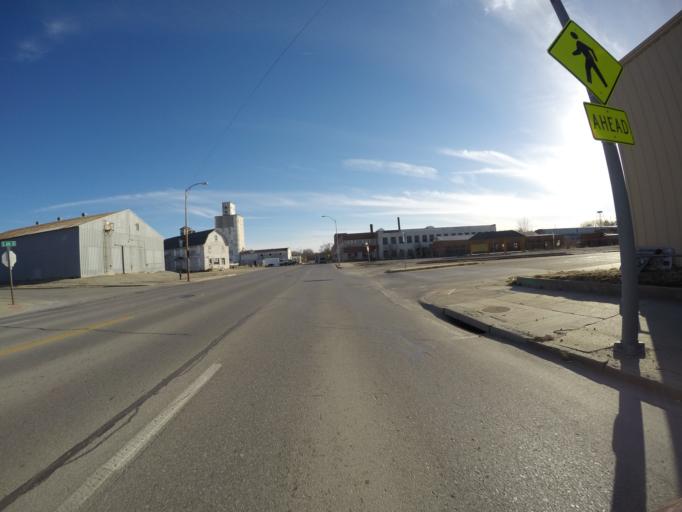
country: US
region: Nebraska
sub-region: Gage County
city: Beatrice
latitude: 40.2612
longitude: -96.7468
